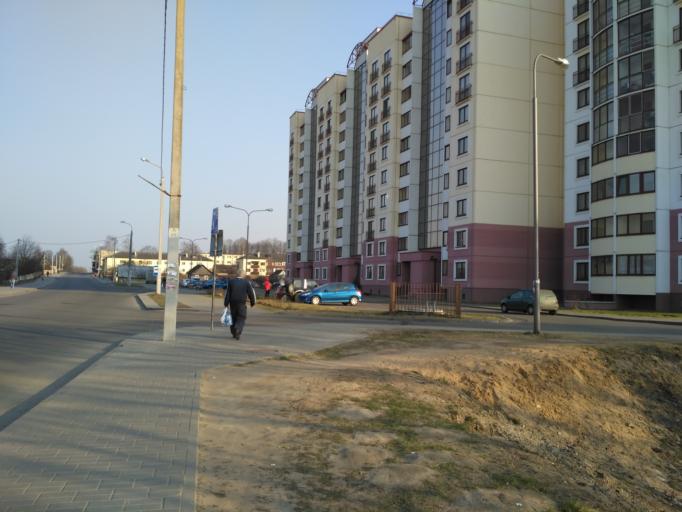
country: BY
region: Minsk
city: Zaslawye
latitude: 54.0088
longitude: 27.2757
